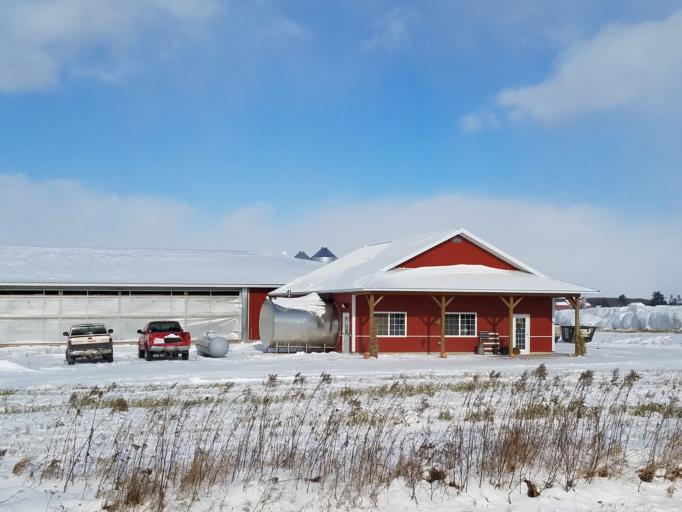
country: US
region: Wisconsin
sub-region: Clark County
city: Loyal
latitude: 44.6109
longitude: -90.4478
